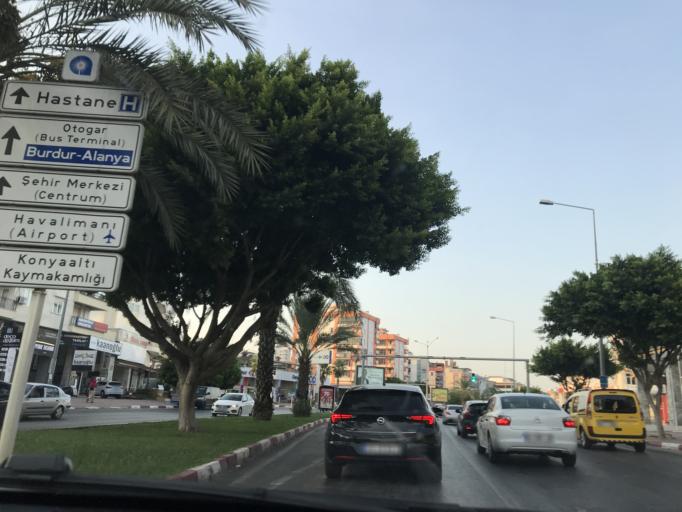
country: TR
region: Antalya
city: Antalya
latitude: 36.8738
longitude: 30.6424
